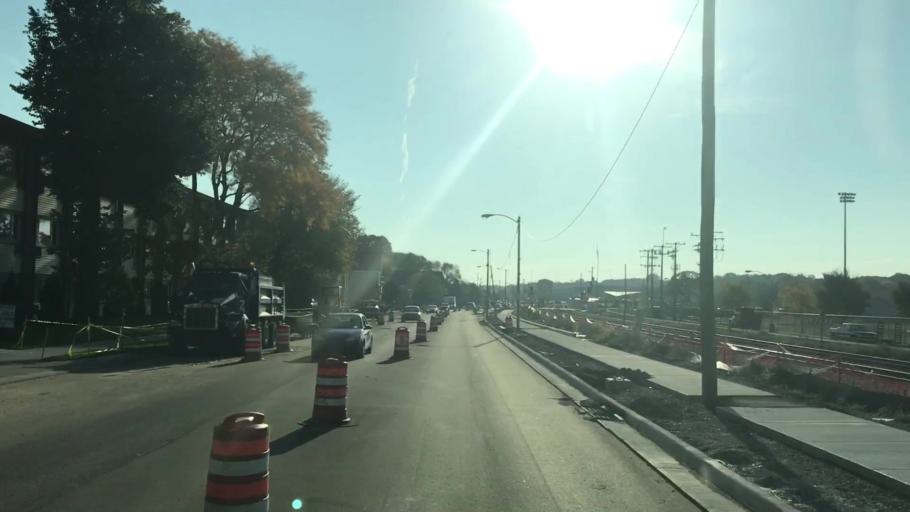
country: US
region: Wisconsin
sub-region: Milwaukee County
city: Wauwatosa
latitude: 43.0485
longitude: -88.0045
